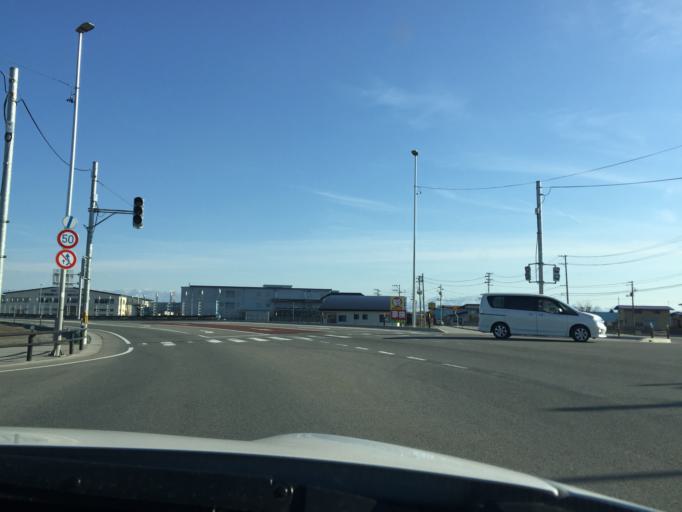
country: JP
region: Yamagata
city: Nagai
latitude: 38.0793
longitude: 140.0385
